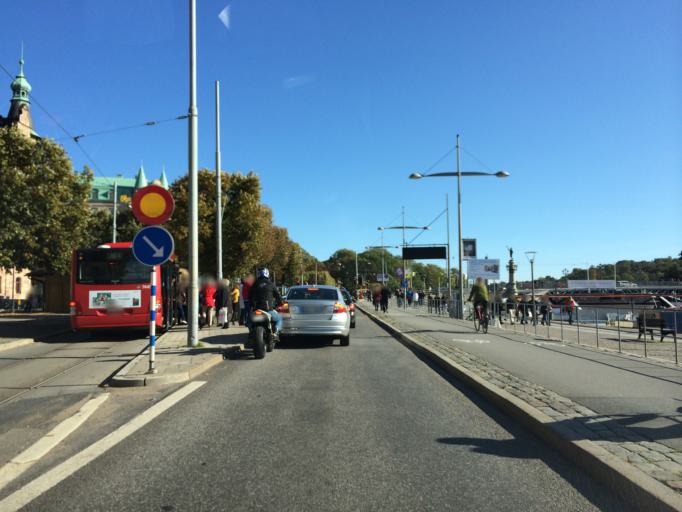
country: SE
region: Stockholm
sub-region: Stockholms Kommun
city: OEstermalm
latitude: 59.3315
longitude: 18.0918
